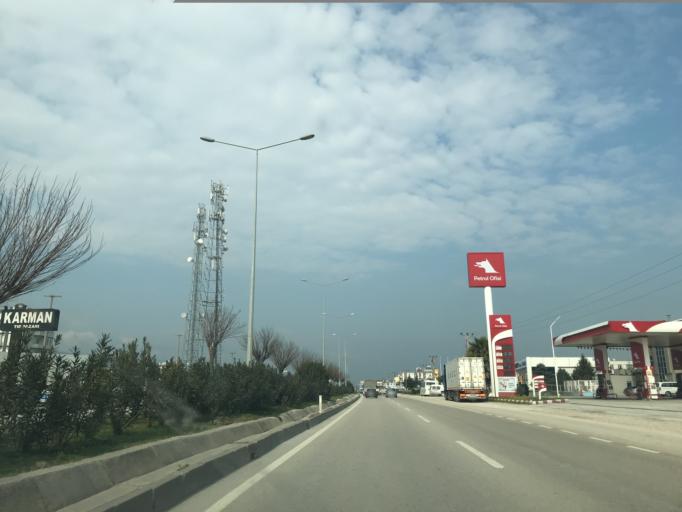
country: TR
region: Hatay
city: Buyuk Dalyan
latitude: 36.2772
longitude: 36.1903
